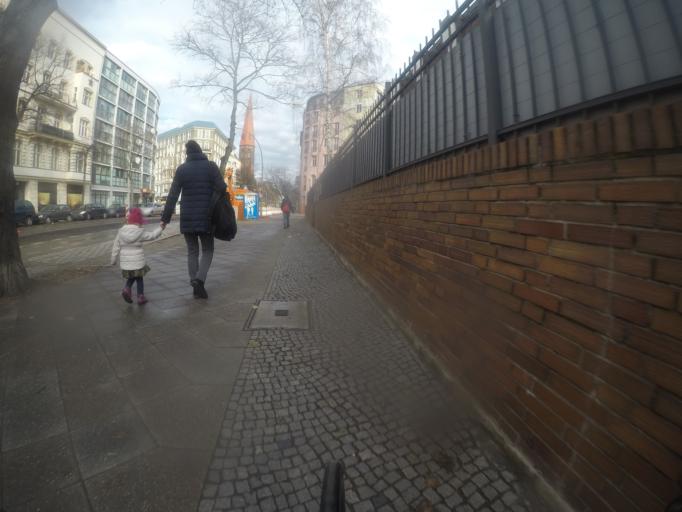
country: DE
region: Berlin
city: Moabit
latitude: 52.5294
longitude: 13.3448
